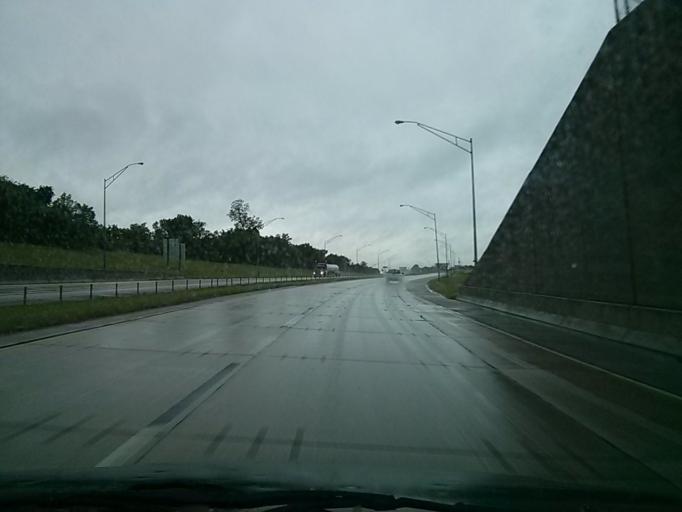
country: US
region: Oklahoma
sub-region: Tulsa County
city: Oakhurst
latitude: 36.1039
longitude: -96.0216
